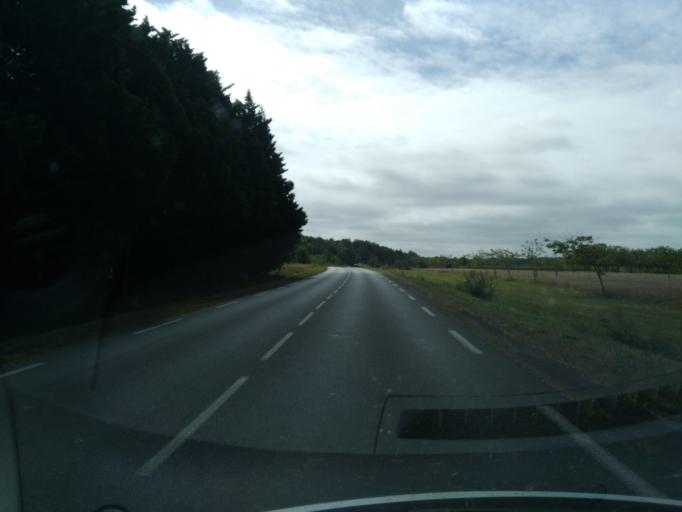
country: FR
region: Poitou-Charentes
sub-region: Departement de la Charente-Maritime
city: Breuillet
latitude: 45.7093
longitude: -1.0639
